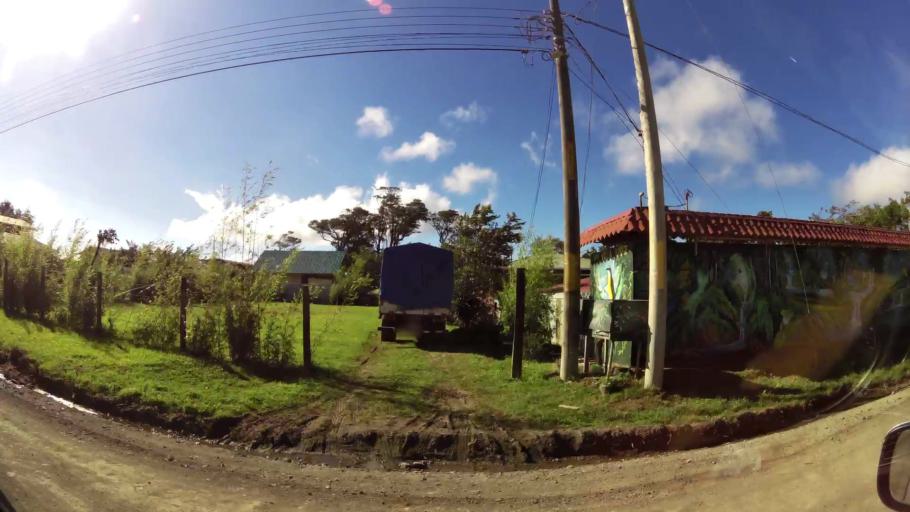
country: CR
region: Guanacaste
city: Juntas
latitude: 10.3149
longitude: -84.8289
